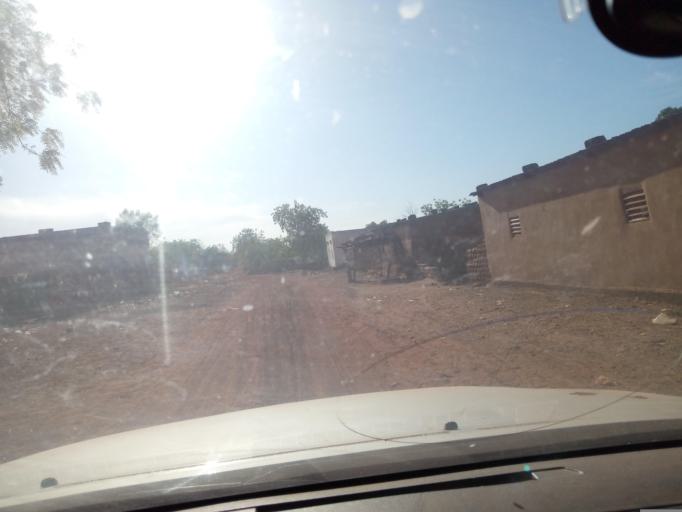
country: ML
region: Sikasso
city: Sikasso
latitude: 11.4857
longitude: -5.4838
